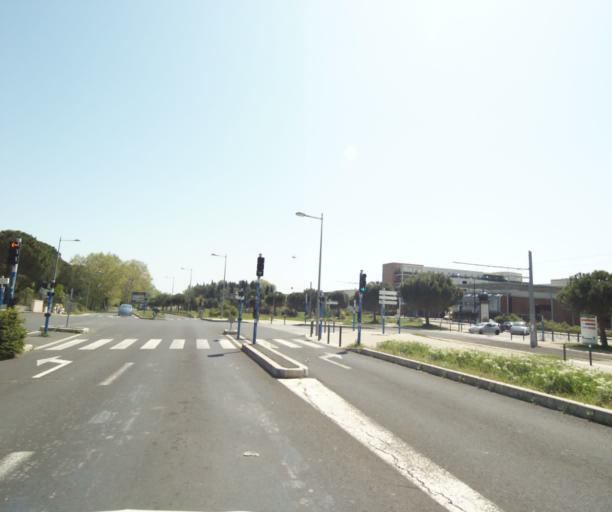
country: FR
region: Languedoc-Roussillon
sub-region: Departement de l'Herault
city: Juvignac
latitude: 43.6347
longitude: 3.8336
